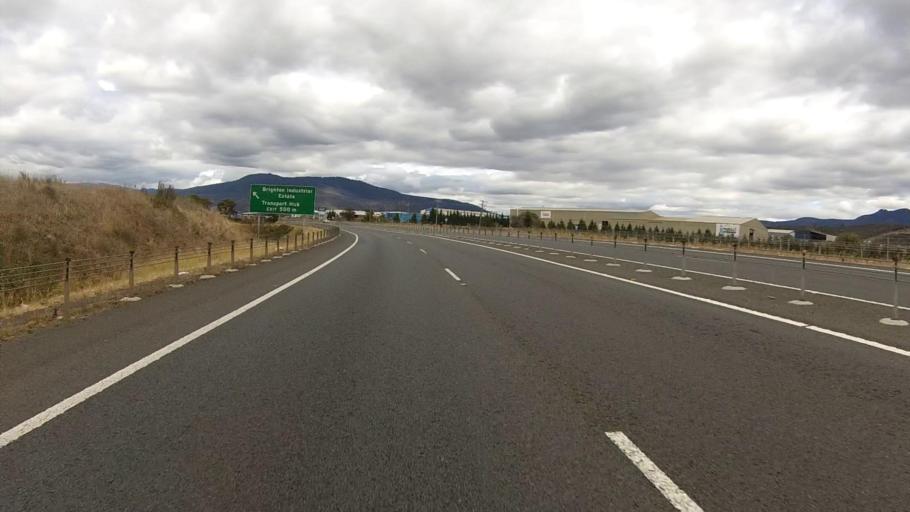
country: AU
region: Tasmania
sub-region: Brighton
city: Bridgewater
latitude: -42.7172
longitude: 147.2398
